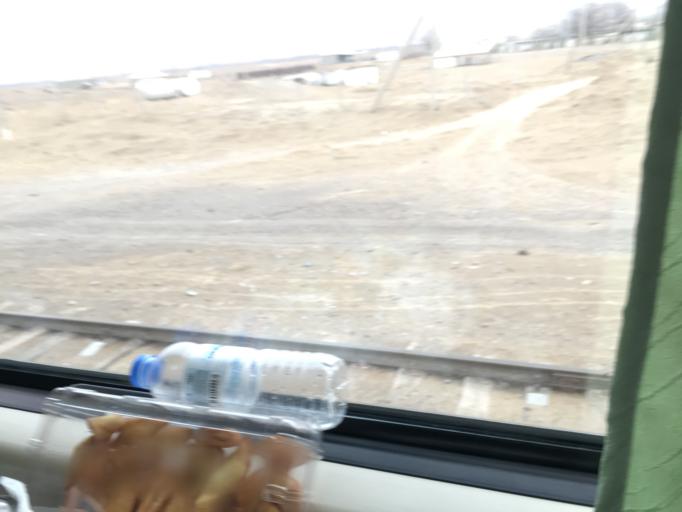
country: AF
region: Badghis
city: Bala Murghab
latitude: 36.2743
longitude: 62.6428
